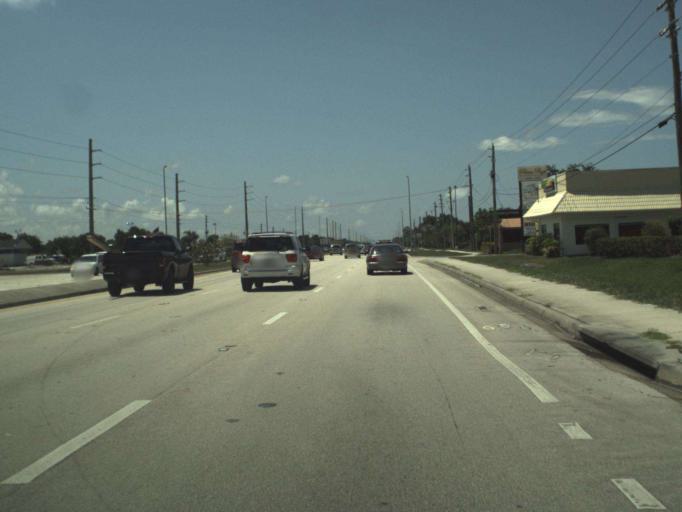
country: US
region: Florida
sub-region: Martin County
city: North River Shores
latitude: 27.2718
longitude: -80.2886
